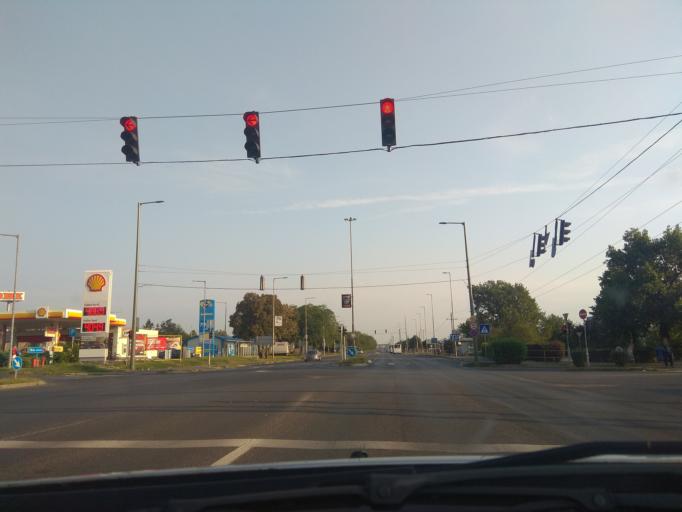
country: HU
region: Borsod-Abauj-Zemplen
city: Szirmabesenyo
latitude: 48.1278
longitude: 20.7840
